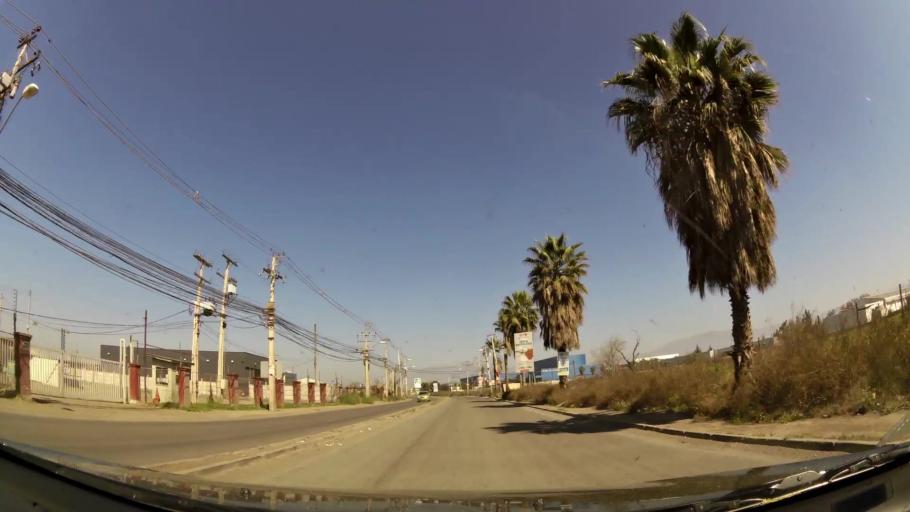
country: CL
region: Santiago Metropolitan
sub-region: Provincia de Chacabuco
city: Chicureo Abajo
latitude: -33.3143
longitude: -70.7260
